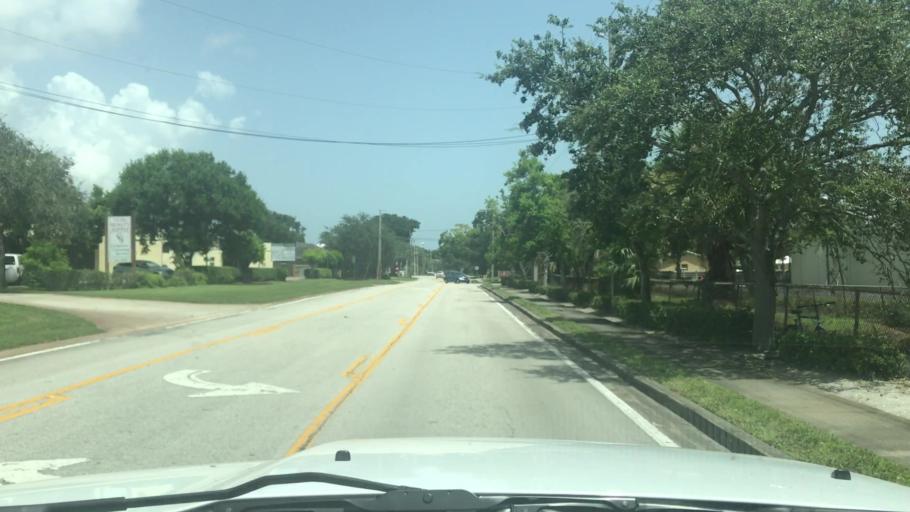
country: US
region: Florida
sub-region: Indian River County
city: Vero Beach
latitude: 27.6302
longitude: -80.3932
